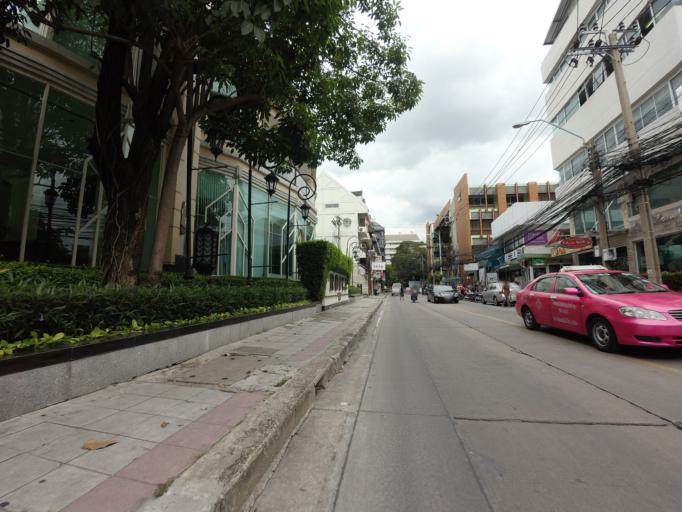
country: TH
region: Bangkok
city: Watthana
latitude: 13.7401
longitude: 100.5659
